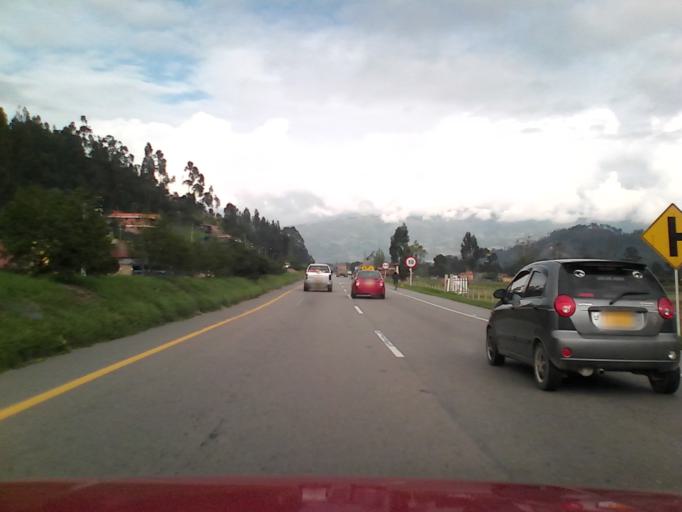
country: CO
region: Boyaca
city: Duitama
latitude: 5.7977
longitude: -72.9995
